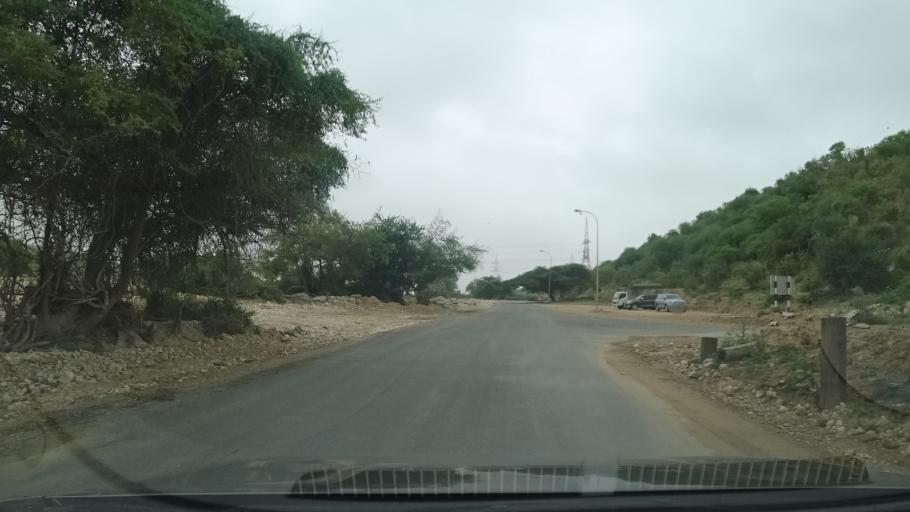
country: OM
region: Zufar
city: Salalah
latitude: 17.1010
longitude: 54.0770
